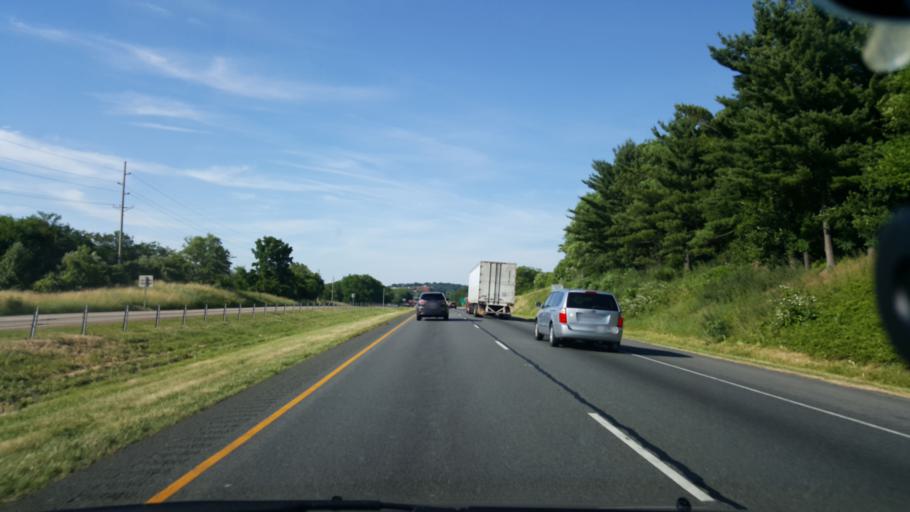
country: US
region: Virginia
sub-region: City of Harrisonburg
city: Harrisonburg
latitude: 38.4197
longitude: -78.8828
